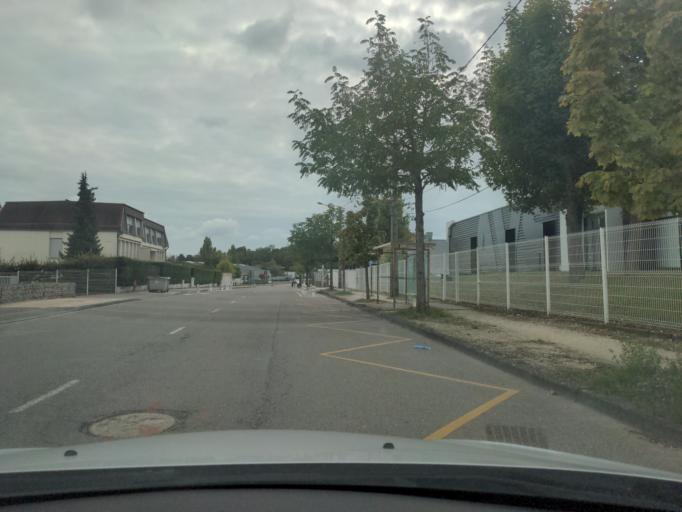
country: FR
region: Bourgogne
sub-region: Departement de la Cote-d'Or
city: Saint-Apollinaire
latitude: 47.3431
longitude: 5.0738
